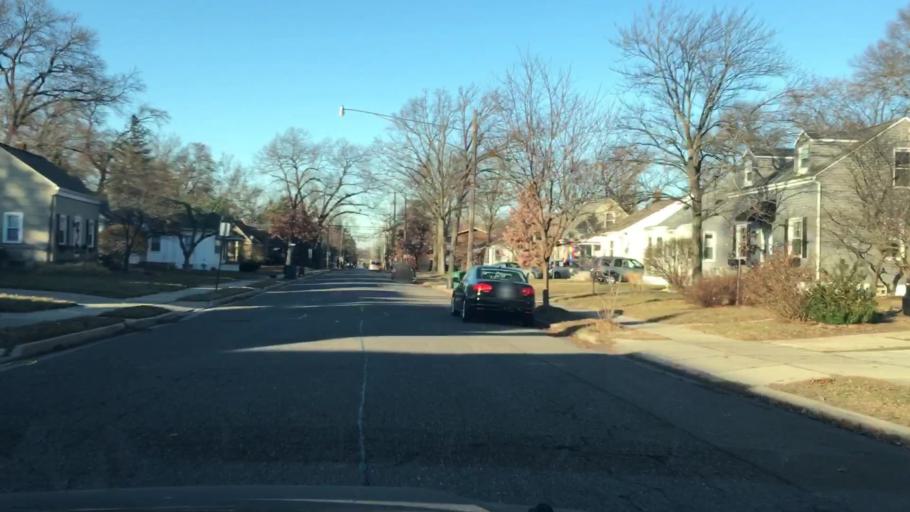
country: US
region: Michigan
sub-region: Oakland County
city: Ferndale
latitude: 42.4530
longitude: -83.1377
